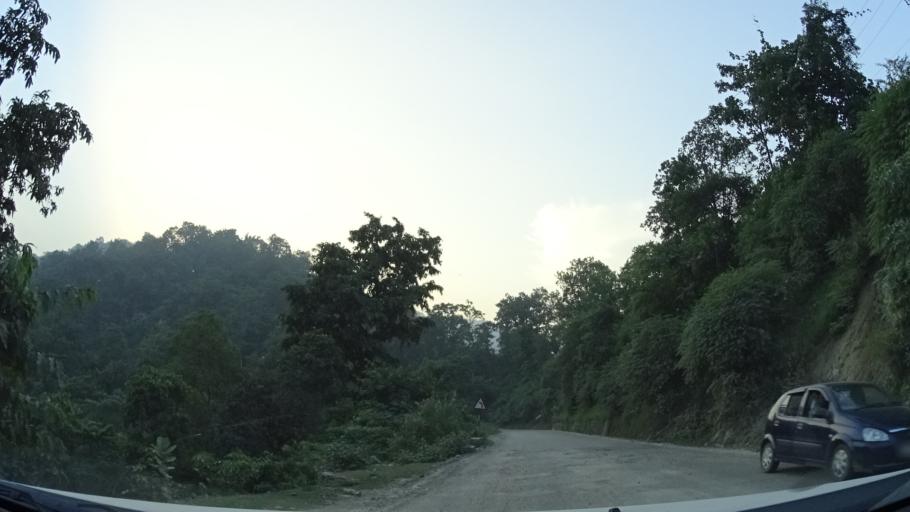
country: IN
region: Uttar Pradesh
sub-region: Maharajganj
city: Nichlaul
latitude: 27.5596
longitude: 83.8481
